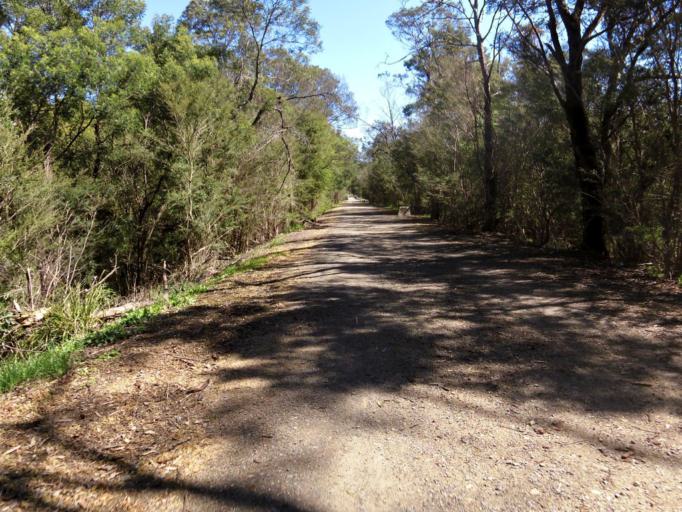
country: AU
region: Victoria
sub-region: Latrobe
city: Moe
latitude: -38.1755
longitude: 146.2741
